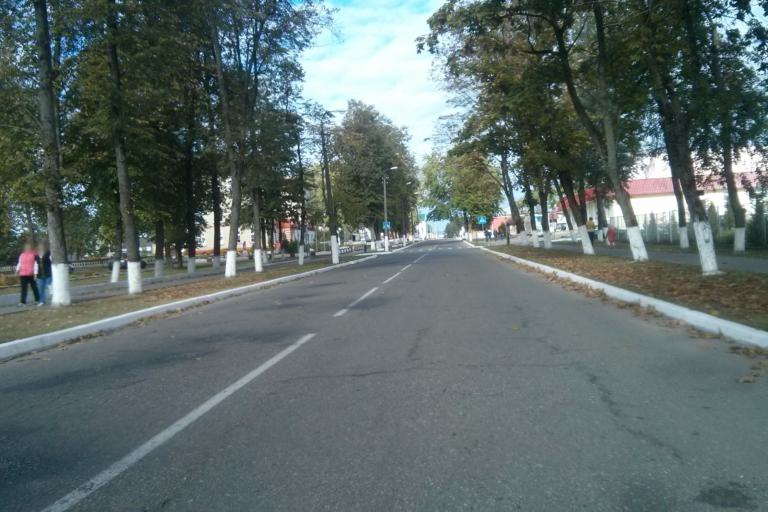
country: BY
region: Minsk
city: Chervyen'
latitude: 53.7121
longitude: 28.4238
